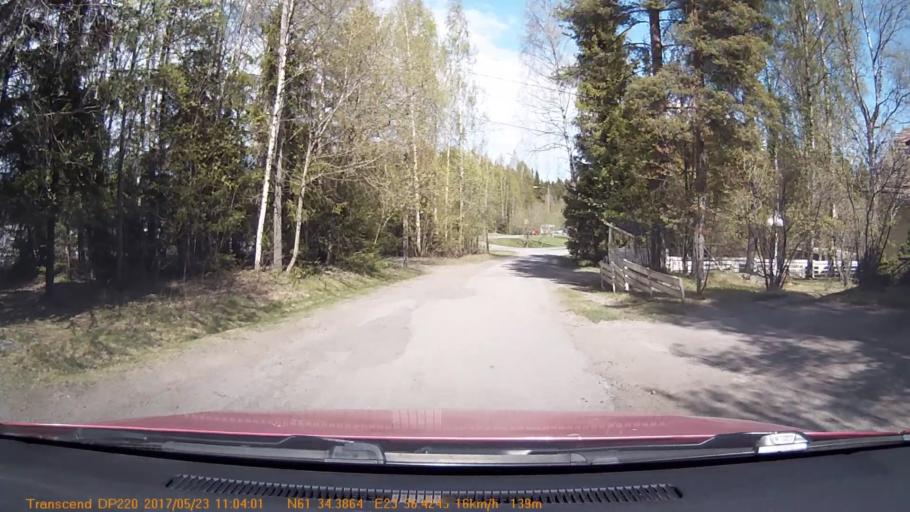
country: FI
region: Pirkanmaa
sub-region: Tampere
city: Yloejaervi
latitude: 61.5730
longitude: 23.6070
